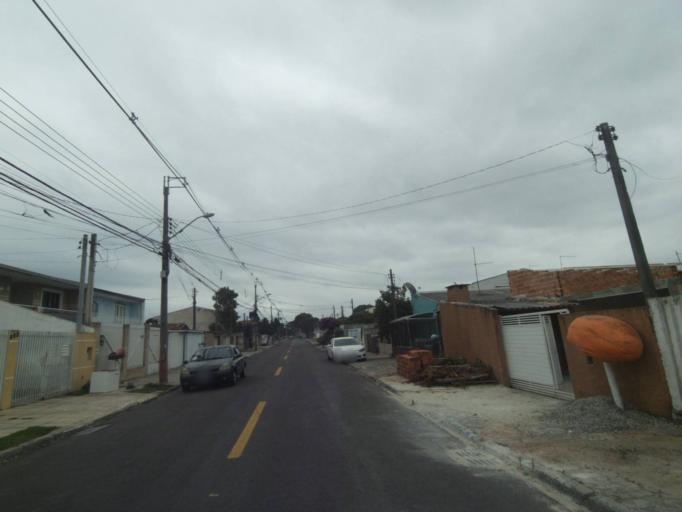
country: BR
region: Parana
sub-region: Sao Jose Dos Pinhais
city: Sao Jose dos Pinhais
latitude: -25.5344
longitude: -49.2613
